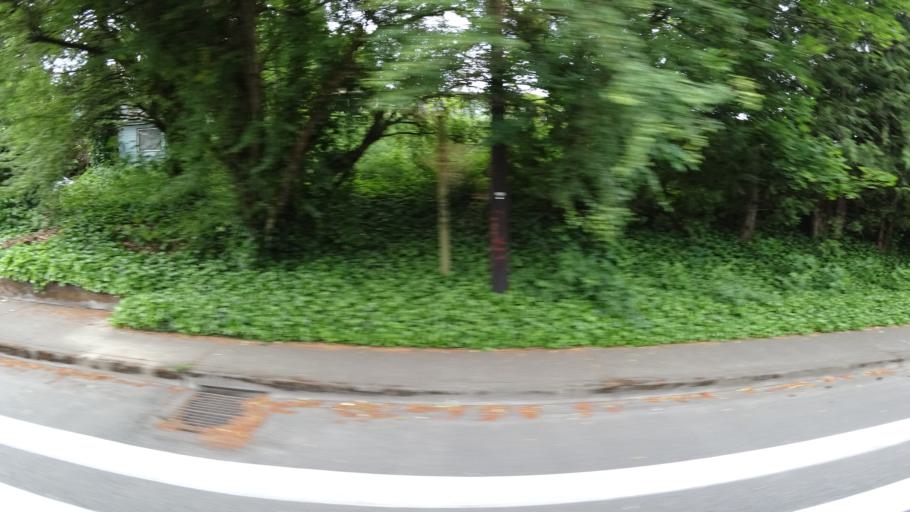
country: US
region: Oregon
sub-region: Washington County
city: Raleigh Hills
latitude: 45.4870
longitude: -122.7361
